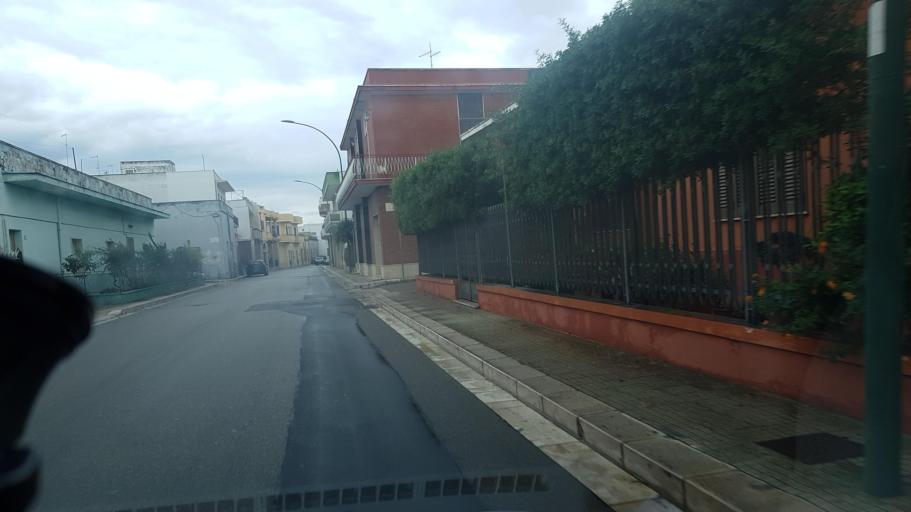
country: IT
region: Apulia
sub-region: Provincia di Lecce
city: Guagnano
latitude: 40.3975
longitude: 17.9533
